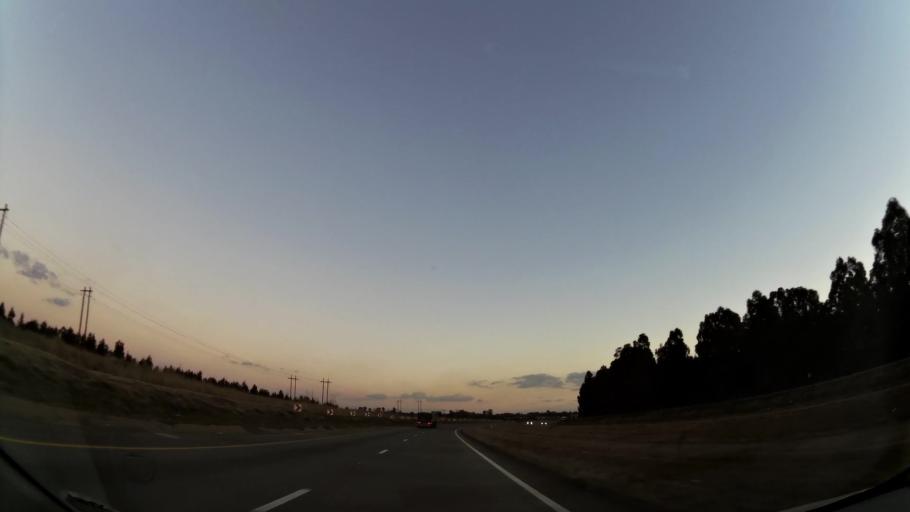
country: ZA
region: Mpumalanga
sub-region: Nkangala District Municipality
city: Witbank
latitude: -25.9580
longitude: 29.1970
